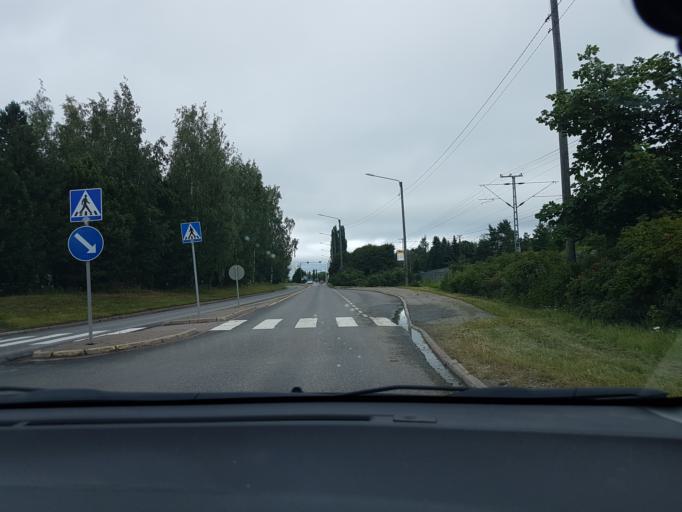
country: FI
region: Uusimaa
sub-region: Helsinki
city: Vantaa
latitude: 60.2715
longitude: 25.0343
